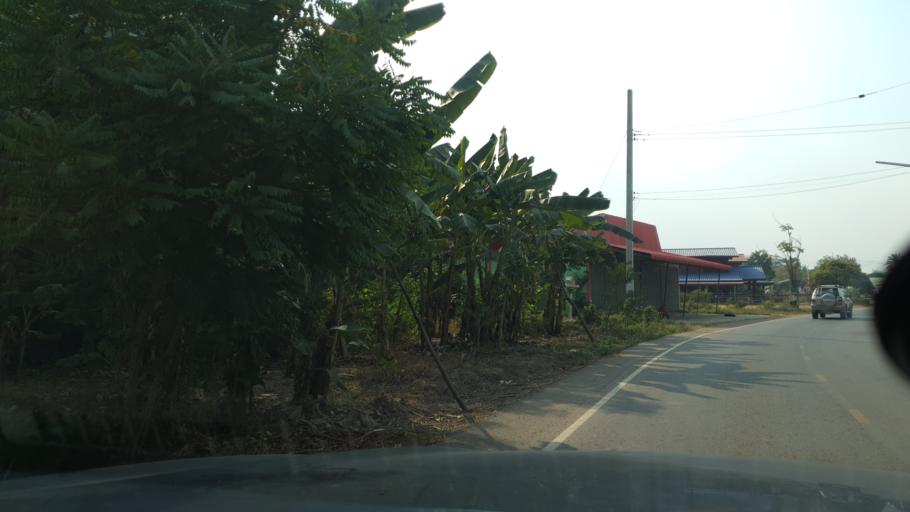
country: TH
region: Sukhothai
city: Ban Dan Lan Hoi
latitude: 17.1163
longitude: 99.5376
